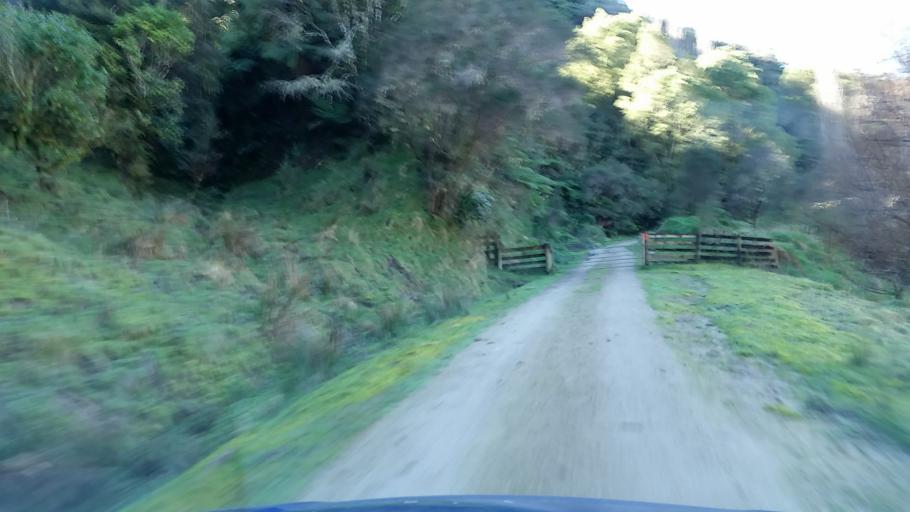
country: NZ
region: Manawatu-Wanganui
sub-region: Wanganui District
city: Wanganui
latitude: -39.6643
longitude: 174.8562
